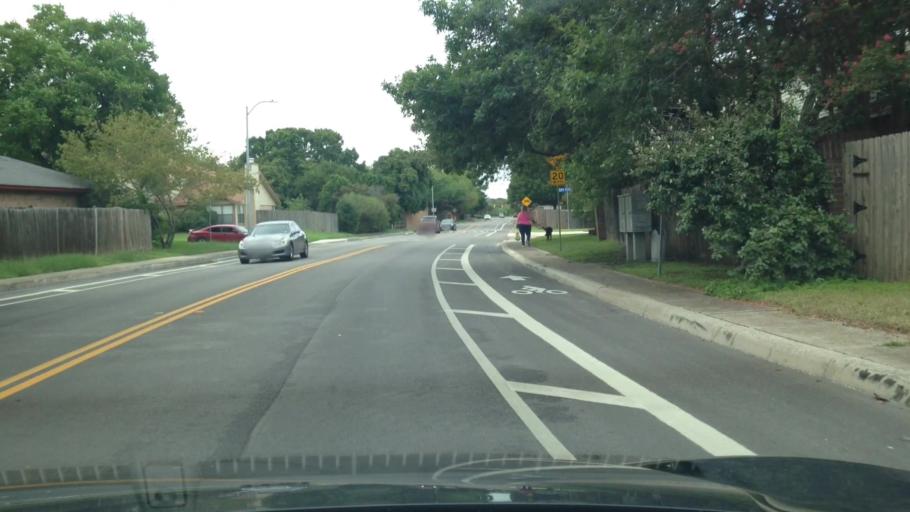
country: US
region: Texas
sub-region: Bexar County
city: Hollywood Park
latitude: 29.5718
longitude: -98.4287
